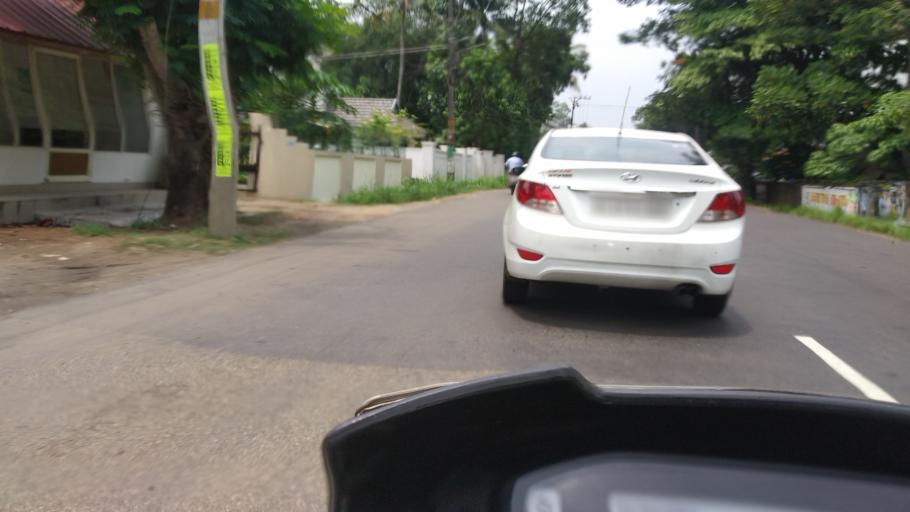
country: IN
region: Kerala
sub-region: Ernakulam
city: Perumpavur
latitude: 10.1163
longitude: 76.4848
